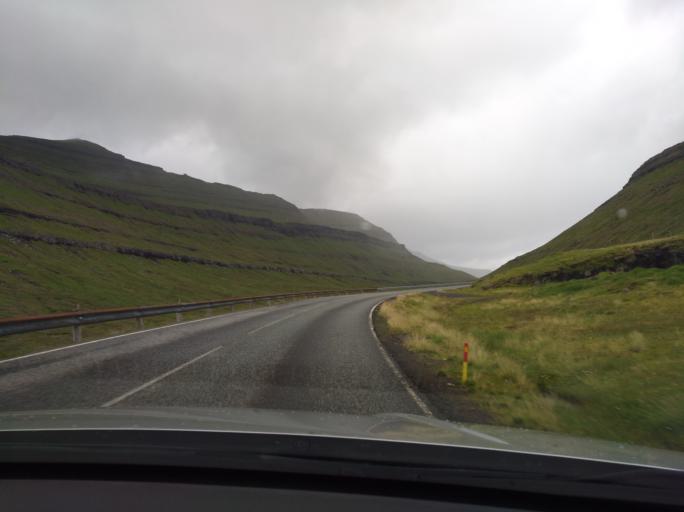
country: FO
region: Eysturoy
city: Fuglafjordur
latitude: 62.2240
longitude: -6.8799
